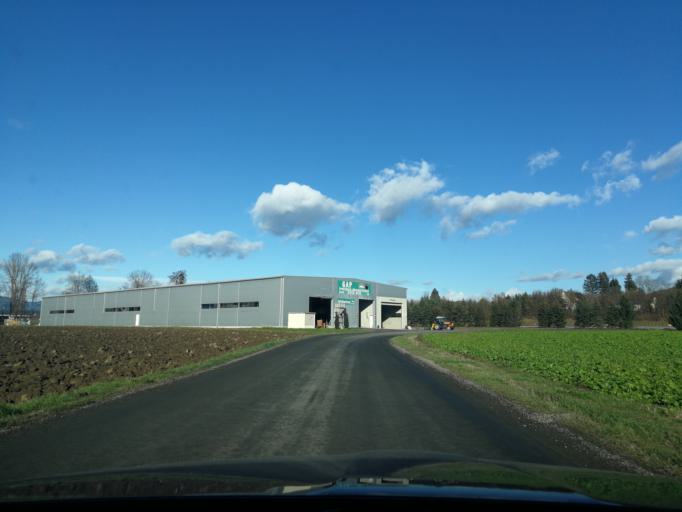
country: AT
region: Styria
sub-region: Politischer Bezirk Weiz
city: Gleisdorf
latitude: 47.1191
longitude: 15.6964
